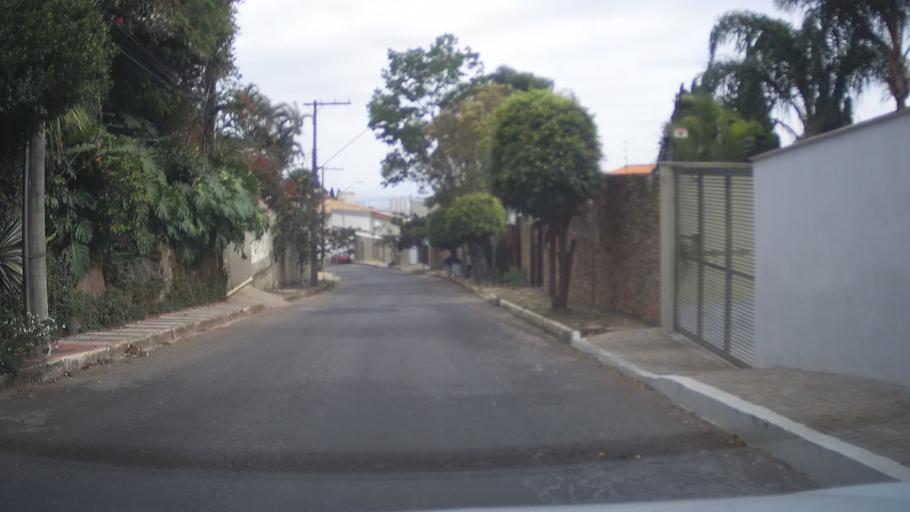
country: BR
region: Minas Gerais
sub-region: Belo Horizonte
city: Belo Horizonte
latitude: -19.9544
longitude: -43.9167
